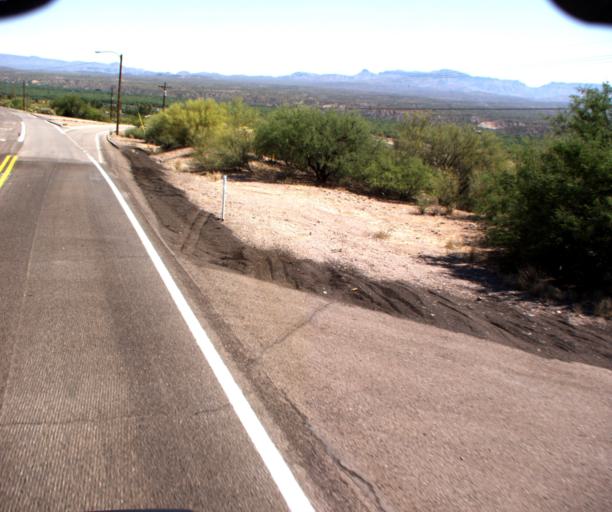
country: US
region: Arizona
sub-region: Pinal County
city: Mammoth
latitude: 32.7111
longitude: -110.6415
